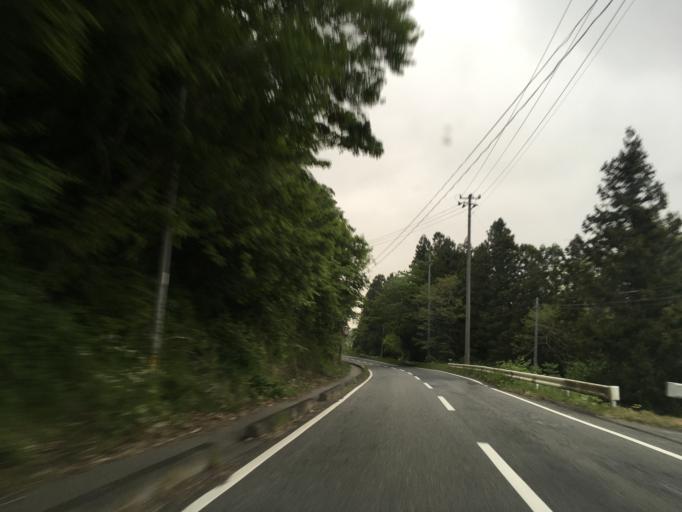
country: JP
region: Miyagi
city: Wakuya
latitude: 38.7307
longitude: 141.2992
